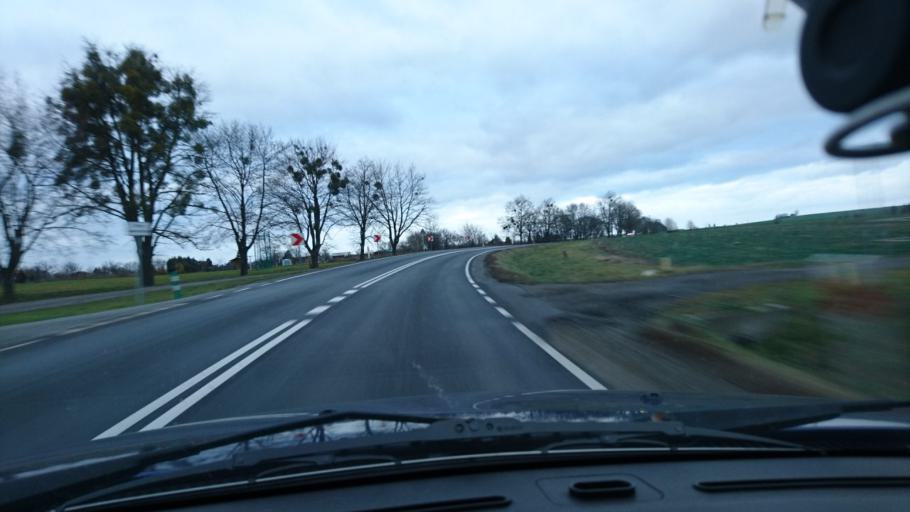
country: PL
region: Opole Voivodeship
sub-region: Powiat kluczborski
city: Byczyna
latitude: 51.0836
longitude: 18.1982
